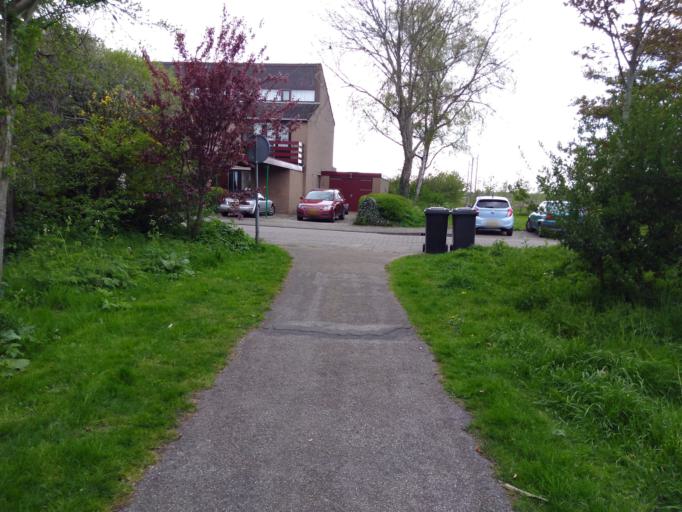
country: NL
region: South Holland
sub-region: Gemeente Leidschendam-Voorburg
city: Voorburg
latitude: 52.1006
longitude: 4.3946
